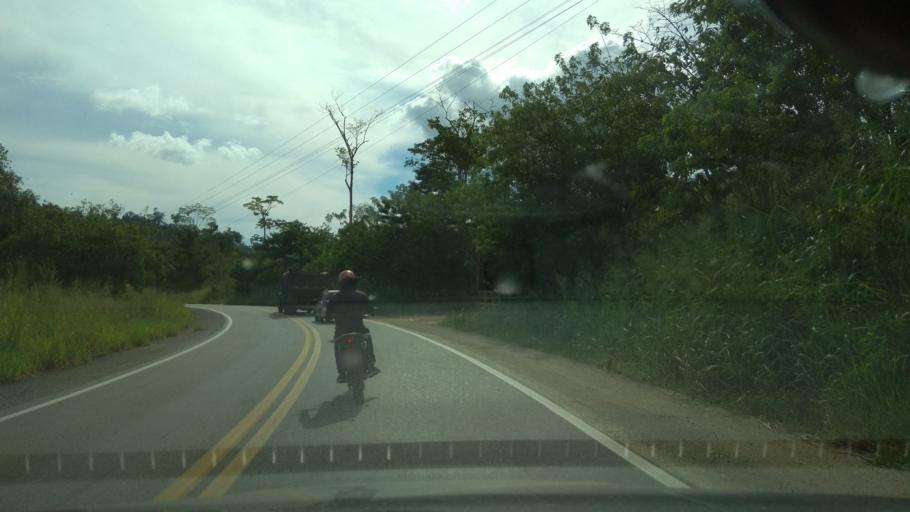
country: BR
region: Bahia
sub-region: Ipiau
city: Ipiau
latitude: -14.0972
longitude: -39.7779
